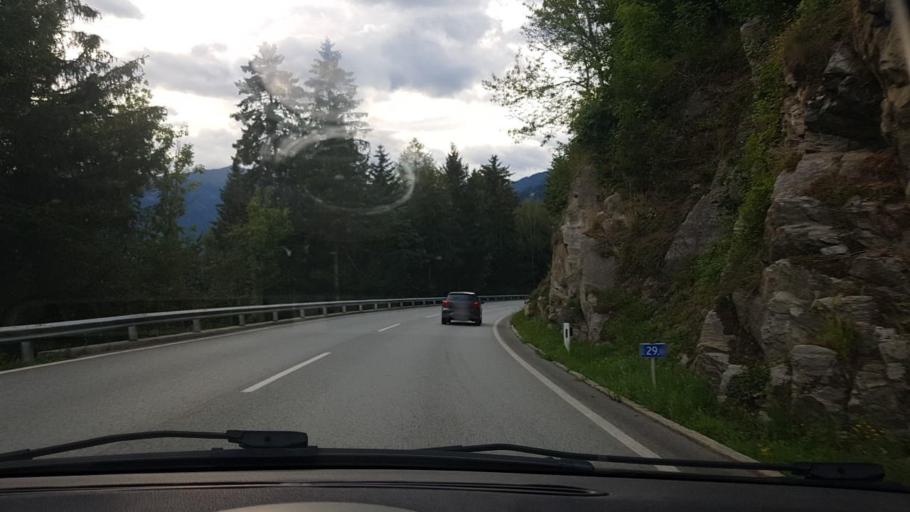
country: AT
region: Tyrol
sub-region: Politischer Bezirk Lienz
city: Dolsach
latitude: 46.8333
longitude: 12.8435
